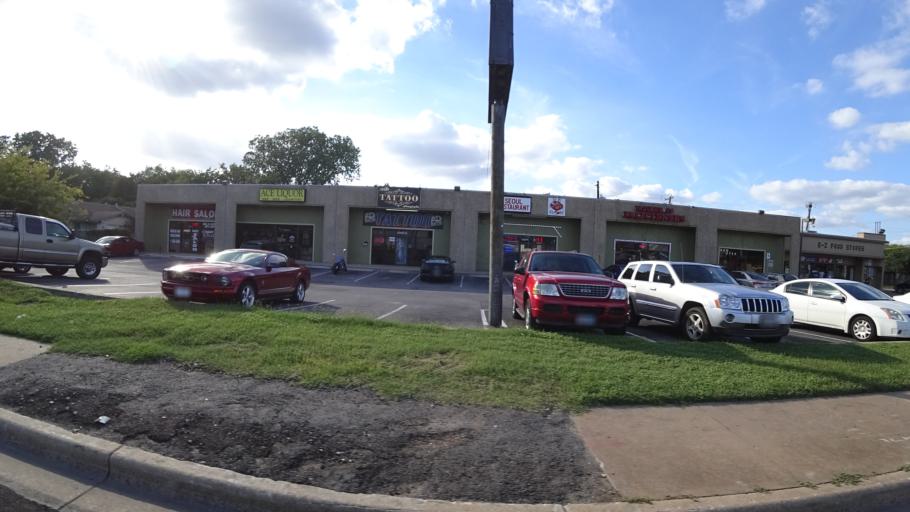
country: US
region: Texas
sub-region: Travis County
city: Onion Creek
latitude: 30.2002
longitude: -97.7860
